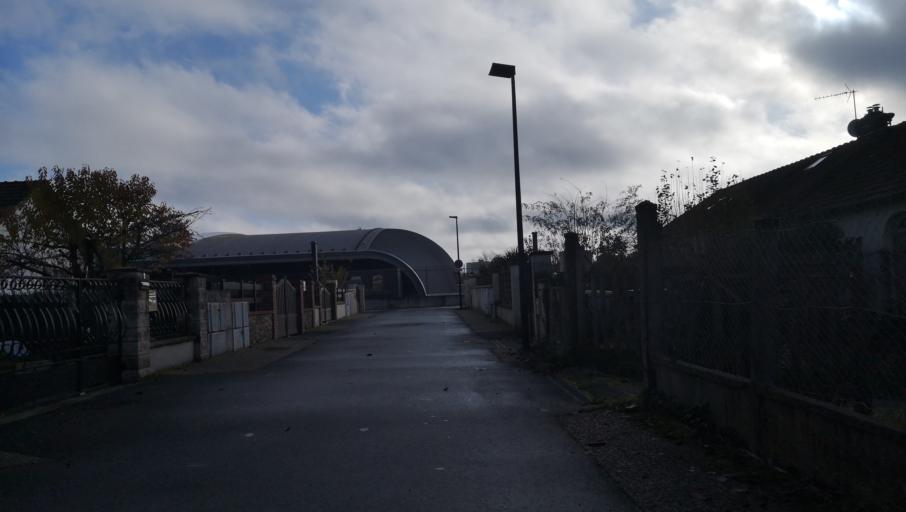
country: FR
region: Centre
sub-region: Departement du Loiret
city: Semoy
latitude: 47.9097
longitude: 1.9393
